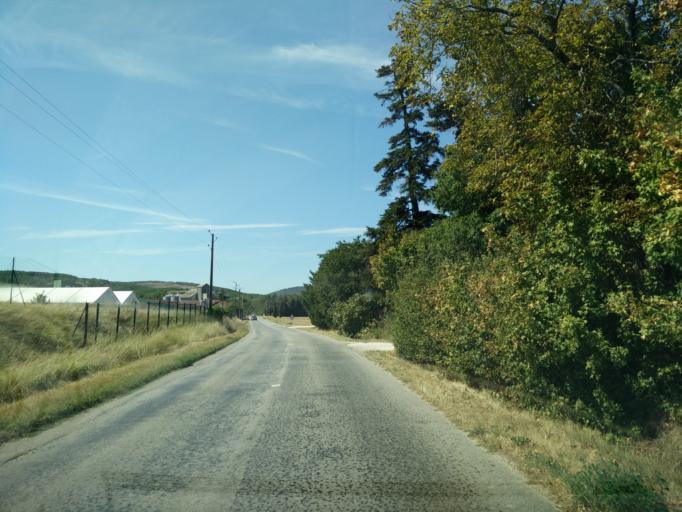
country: FR
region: Rhone-Alpes
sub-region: Departement de la Drome
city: Montboucher-sur-Jabron
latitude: 44.5494
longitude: 4.8493
